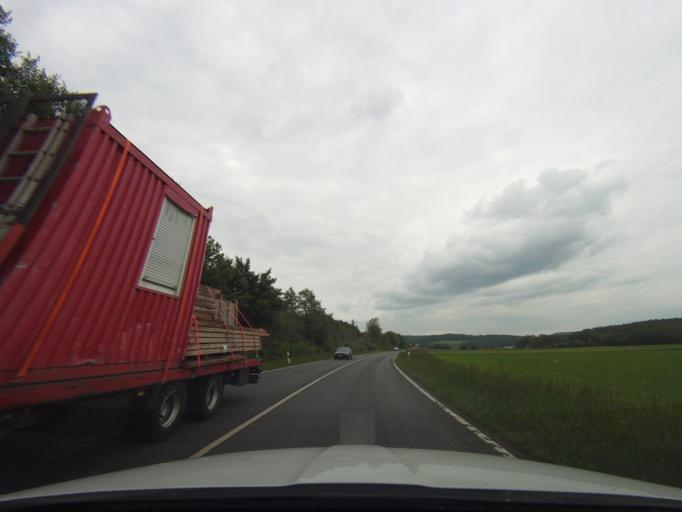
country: DE
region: Bavaria
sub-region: Upper Franconia
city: Weismain
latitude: 50.1037
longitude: 11.2370
